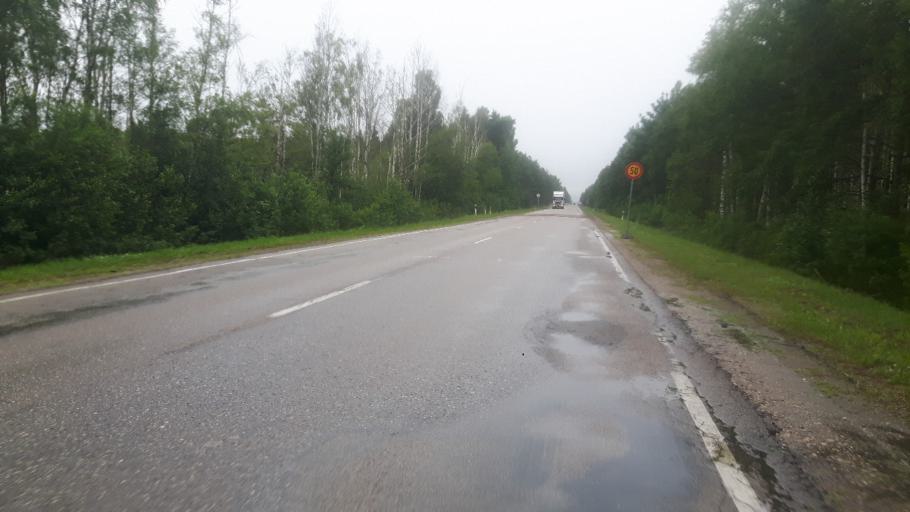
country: LV
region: Rucavas
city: Rucava
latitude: 56.1413
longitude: 21.1520
